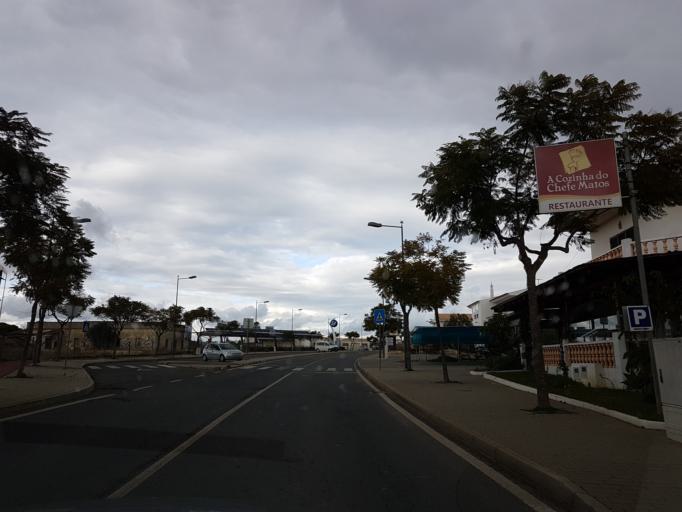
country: PT
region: Faro
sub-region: Albufeira
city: Ferreiras
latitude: 37.1078
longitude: -8.2310
